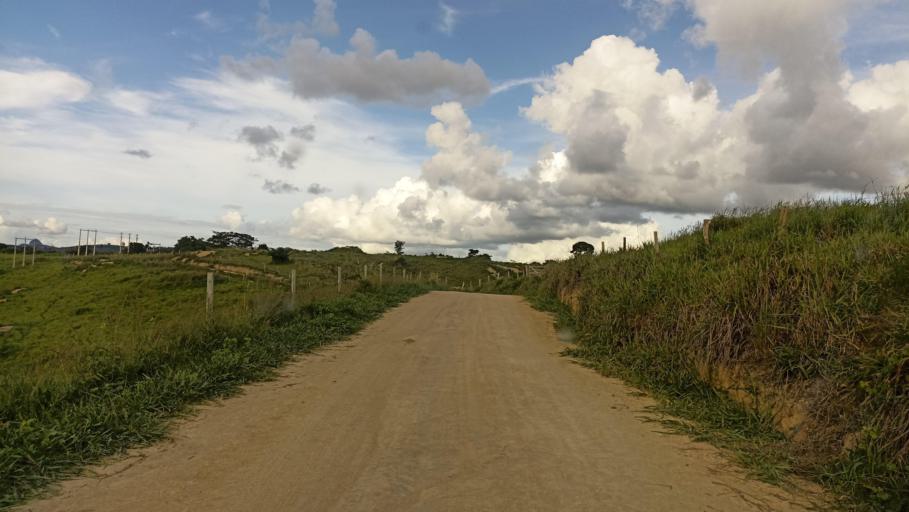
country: BR
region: Minas Gerais
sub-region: Almenara
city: Almenara
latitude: -16.5465
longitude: -40.4499
